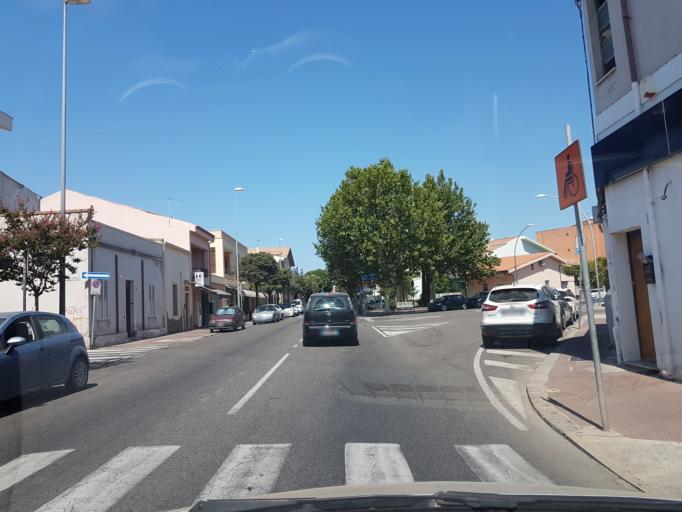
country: IT
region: Sardinia
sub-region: Provincia di Oristano
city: Oristano
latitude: 39.8969
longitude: 8.5952
